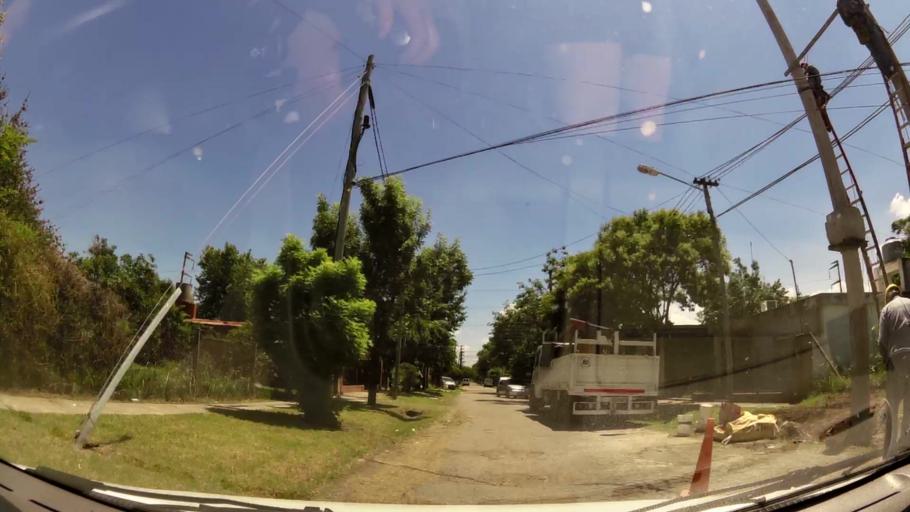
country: AR
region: Buenos Aires
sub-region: Partido de Merlo
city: Merlo
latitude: -34.6458
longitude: -58.7088
